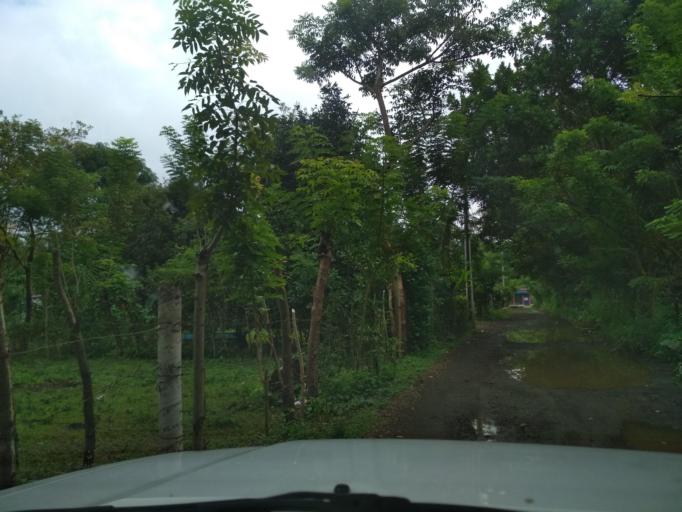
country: MX
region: Veracruz
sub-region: San Andres Tuxtla
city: Matacapan
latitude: 18.4368
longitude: -95.1650
